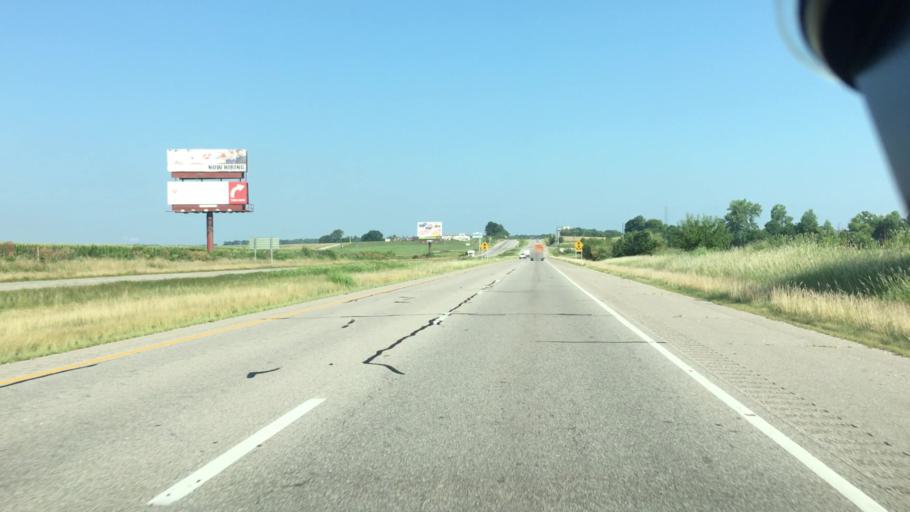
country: US
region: Indiana
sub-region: Gibson County
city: Princeton
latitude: 38.3229
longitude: -87.5792
